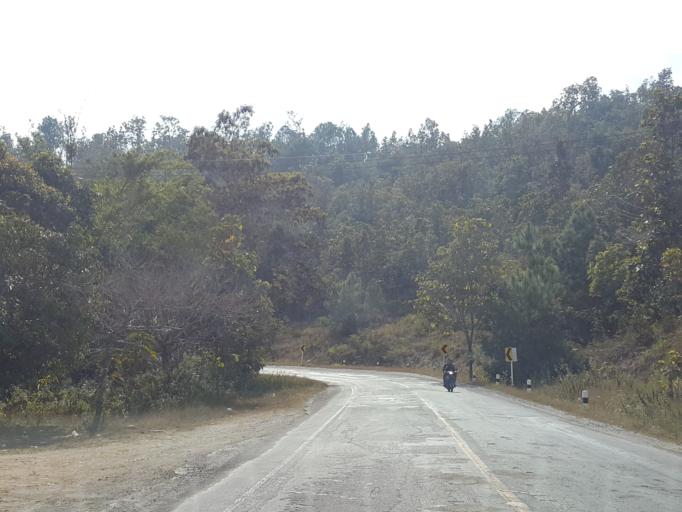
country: TH
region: Chiang Mai
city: Om Koi
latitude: 17.8099
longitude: 98.3630
